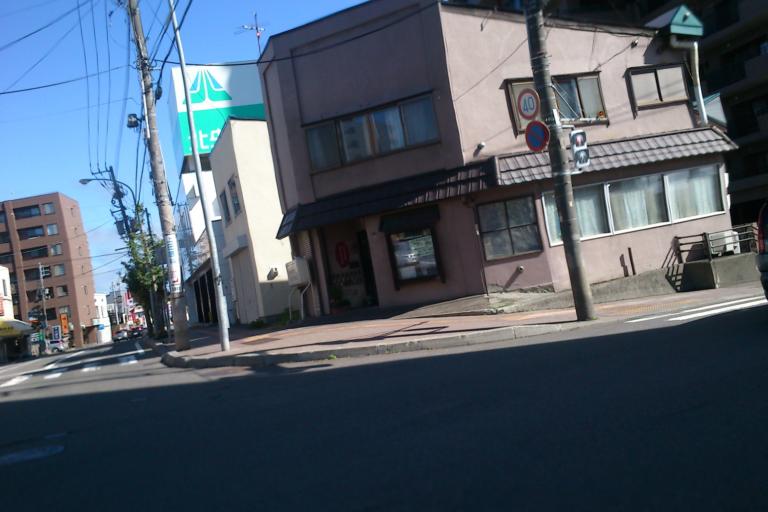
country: JP
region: Hokkaido
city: Sapporo
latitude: 43.1181
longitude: 141.2436
